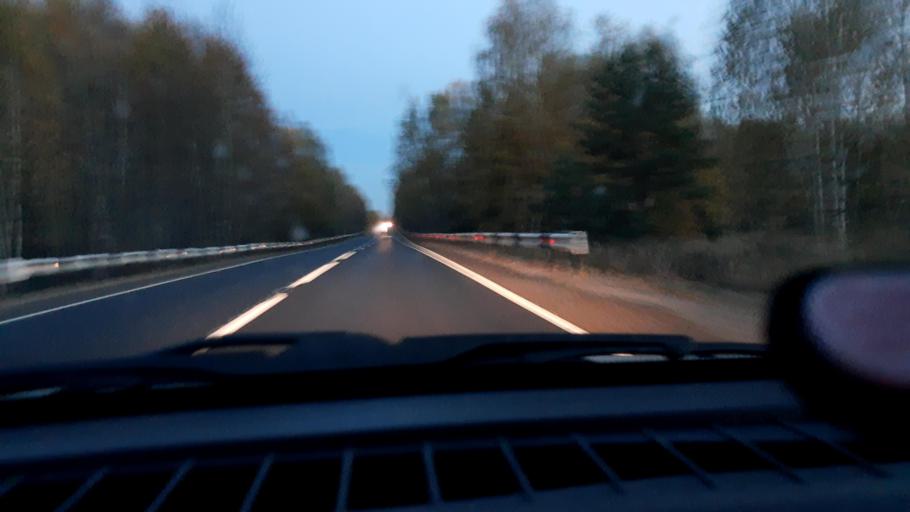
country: RU
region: Nizjnij Novgorod
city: Novaya Balakhna
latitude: 56.5687
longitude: 43.7139
